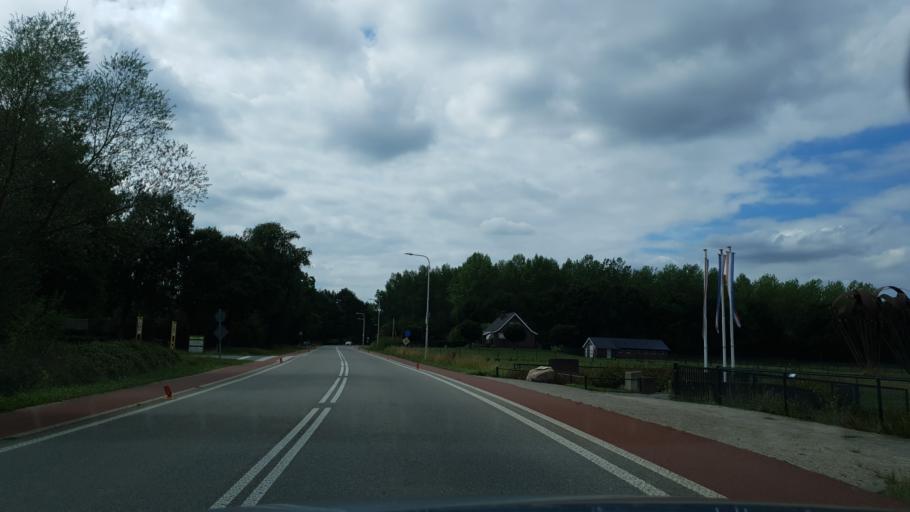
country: NL
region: North Brabant
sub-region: Gemeente Grave
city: Grave
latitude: 51.7683
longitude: 5.7706
